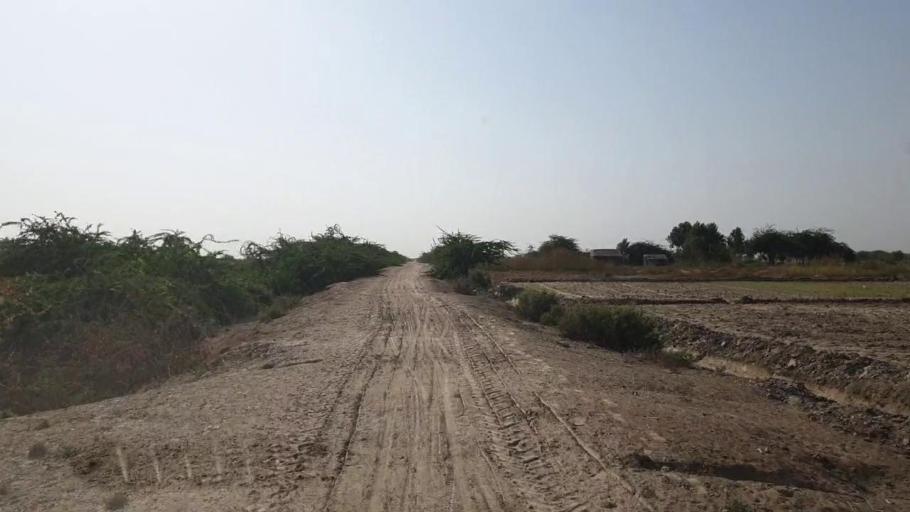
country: PK
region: Sindh
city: Kadhan
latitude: 24.5771
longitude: 69.0807
